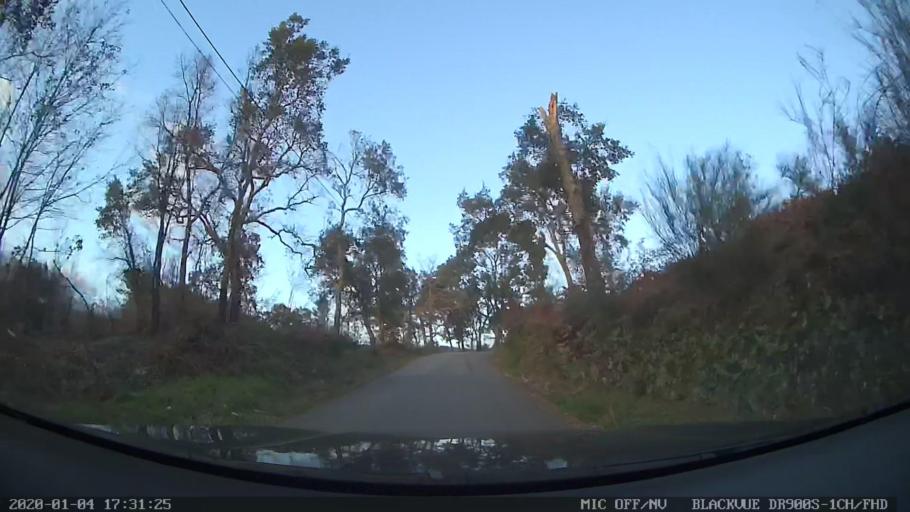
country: PT
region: Vila Real
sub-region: Mondim de Basto
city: Mondim de Basto
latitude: 41.4281
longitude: -7.9849
